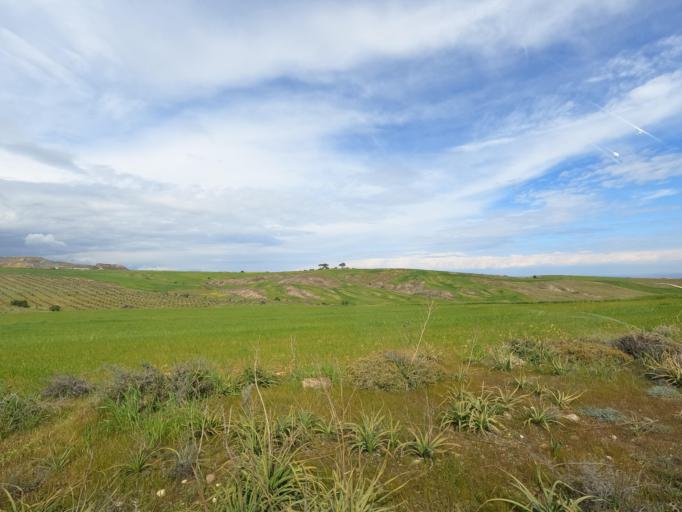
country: CY
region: Lefkosia
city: Lefka
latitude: 35.0915
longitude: 32.9297
